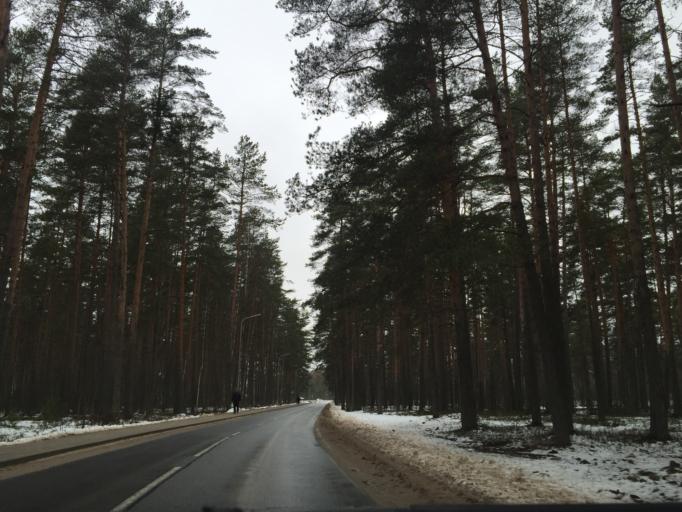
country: LV
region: Garkalne
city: Garkalne
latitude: 57.0418
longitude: 24.4279
